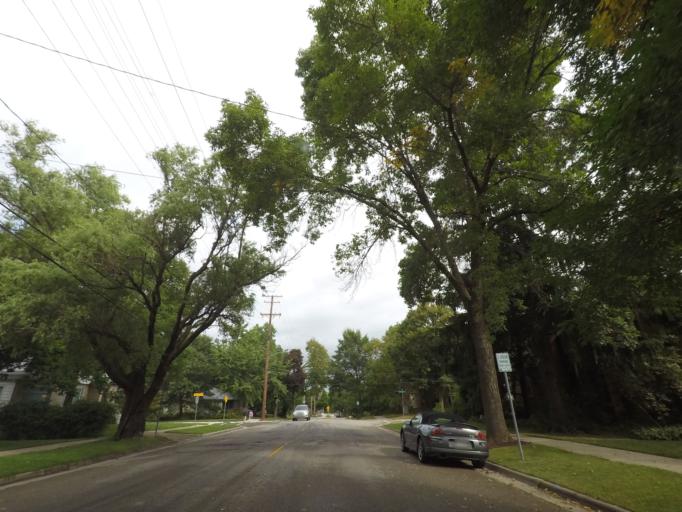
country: US
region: Wisconsin
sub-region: Dane County
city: Shorewood Hills
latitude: 43.0698
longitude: -89.4363
